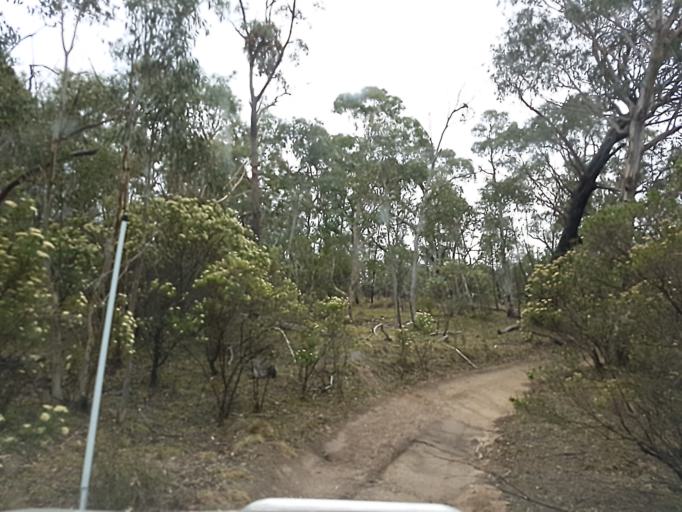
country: AU
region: New South Wales
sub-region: Snowy River
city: Jindabyne
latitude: -36.8885
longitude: 148.3373
